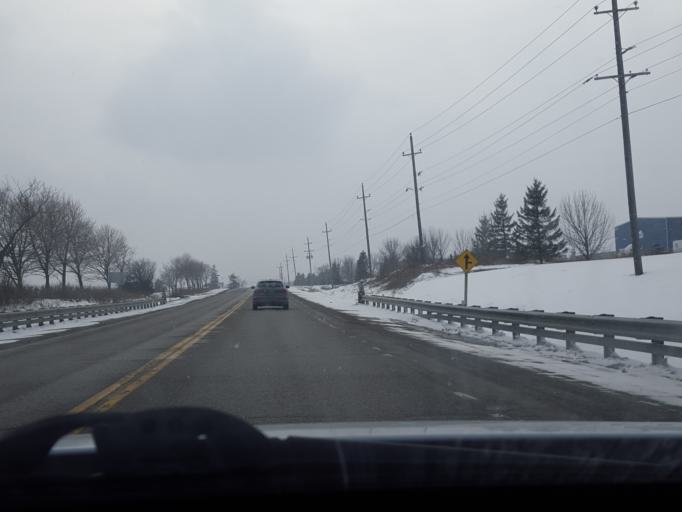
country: CA
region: Ontario
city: Uxbridge
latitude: 44.0196
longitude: -79.2281
